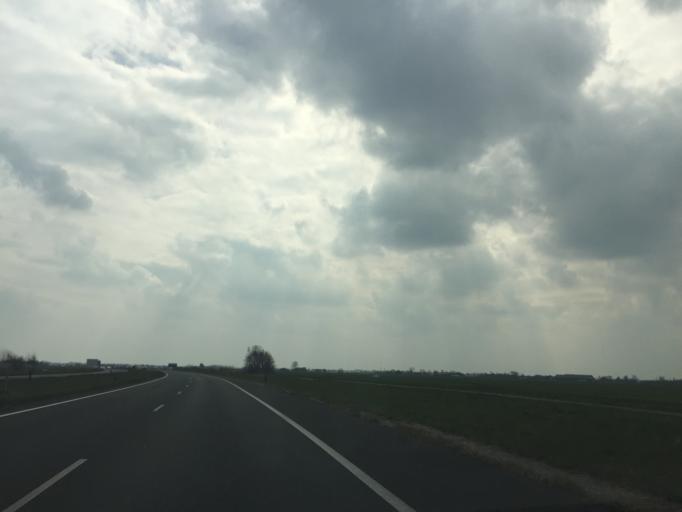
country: NL
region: South Holland
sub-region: Gemeente Alphen aan den Rijn
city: Alphen aan den Rijn
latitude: 52.1156
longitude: 4.6354
